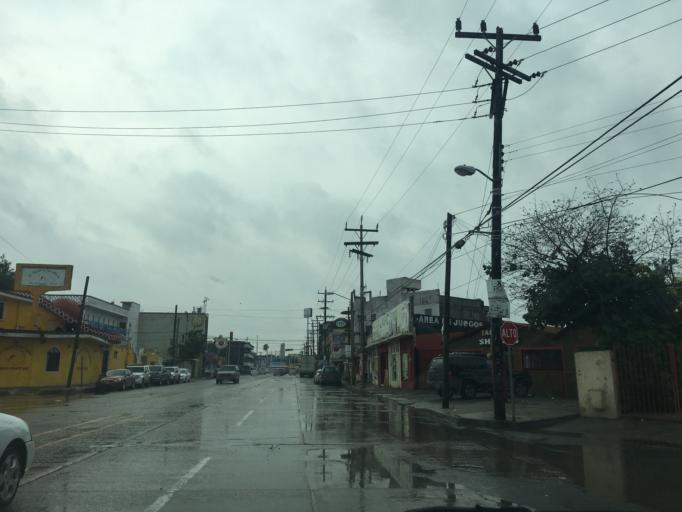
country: MX
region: Tamaulipas
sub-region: Matamoros
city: Heroica Matamoros
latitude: 25.8722
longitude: -97.5063
